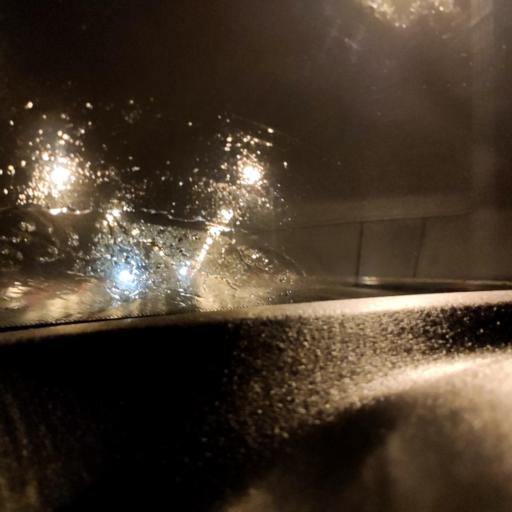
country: RU
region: Samara
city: Novosemeykino
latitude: 53.3384
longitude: 50.2324
